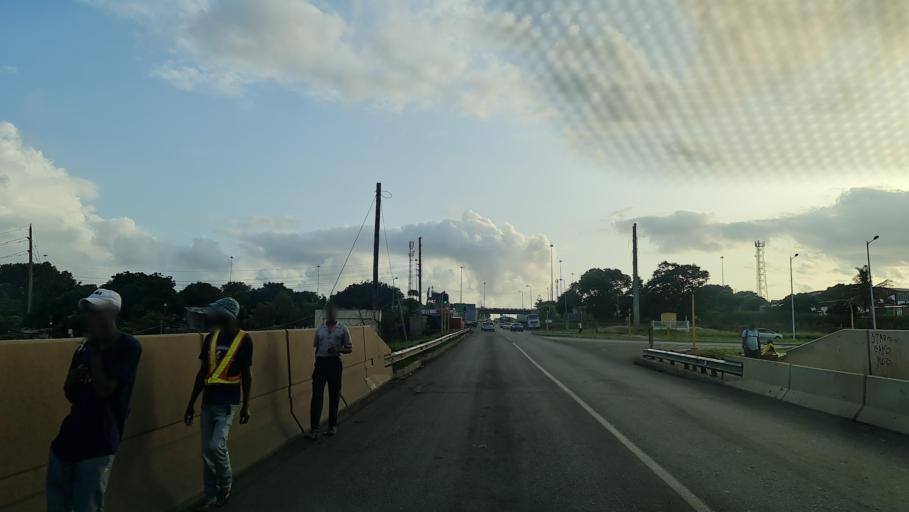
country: MZ
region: Maputo City
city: Maputo
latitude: -25.9462
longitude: 32.5381
